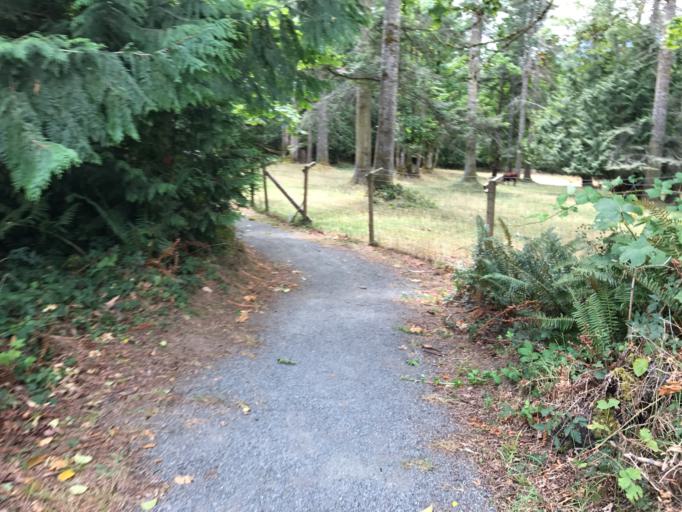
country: CA
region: British Columbia
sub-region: Cowichan Valley Regional District
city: Ladysmith
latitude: 48.9296
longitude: -123.7427
